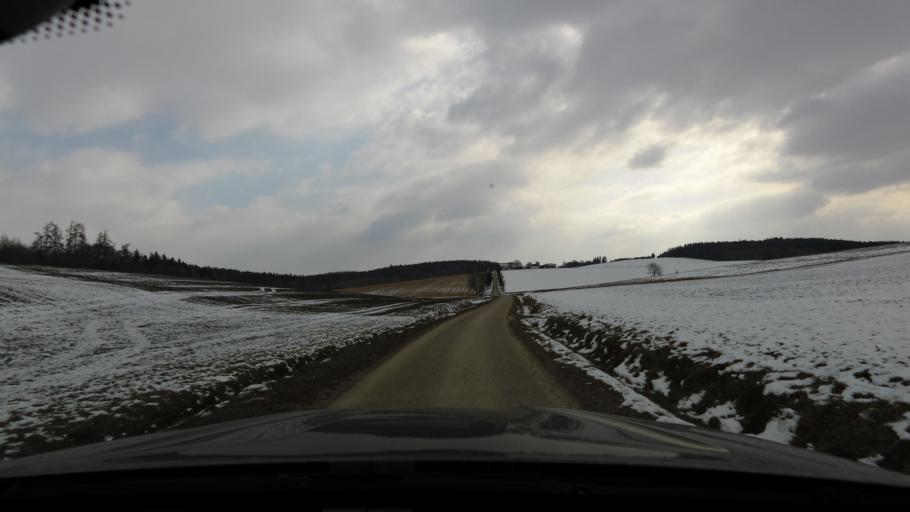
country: DE
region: Bavaria
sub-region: Lower Bavaria
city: Eching
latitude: 48.4671
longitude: 12.0519
